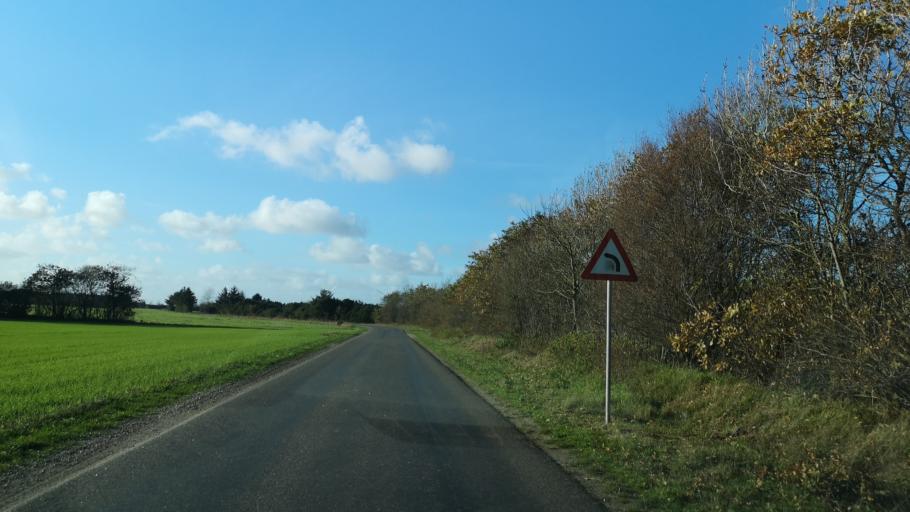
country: DK
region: Central Jutland
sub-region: Ringkobing-Skjern Kommune
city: Skjern
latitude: 55.8354
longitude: 8.3669
